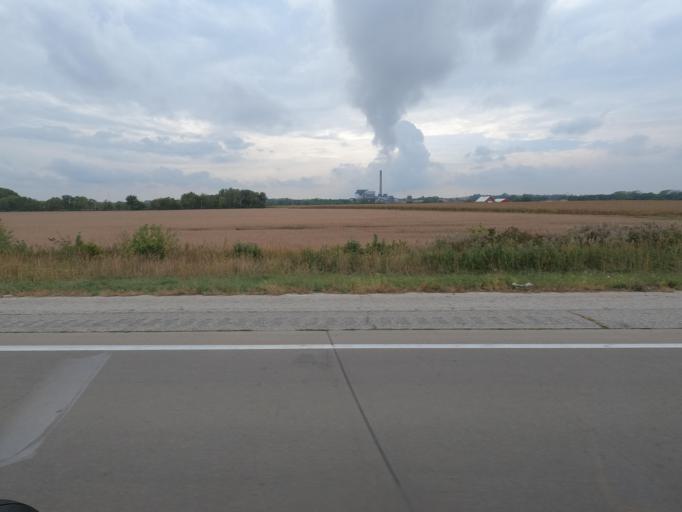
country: US
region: Iowa
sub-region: Wapello County
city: Eddyville
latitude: 41.1098
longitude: -92.5380
